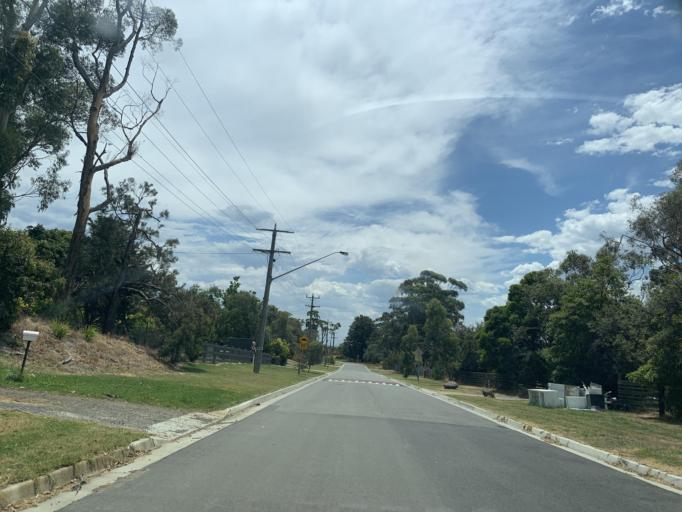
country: AU
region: Victoria
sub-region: Casey
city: Cranbourne South
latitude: -38.1310
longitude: 145.2411
